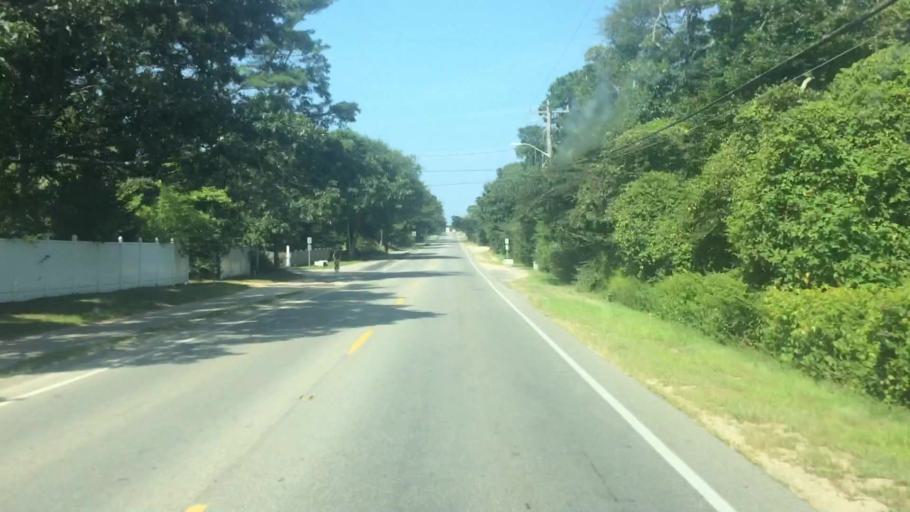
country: US
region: Massachusetts
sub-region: Dukes County
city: Edgartown
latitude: 41.3969
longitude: -70.5368
